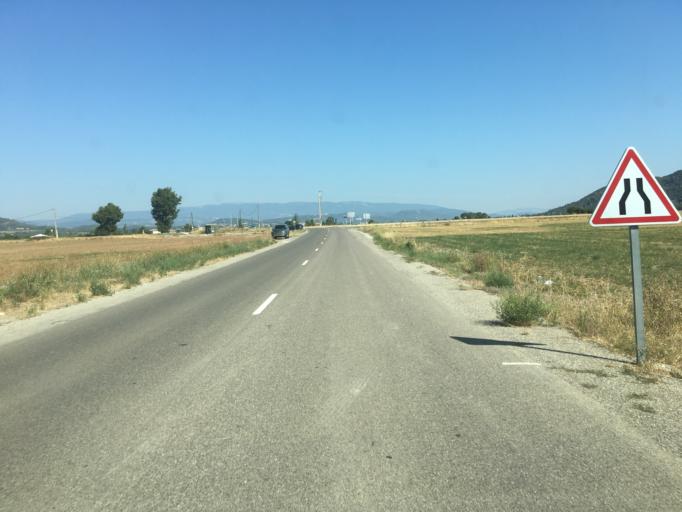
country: FR
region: Provence-Alpes-Cote d'Azur
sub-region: Departement des Alpes-de-Haute-Provence
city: Oraison
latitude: 43.8837
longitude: 5.9087
